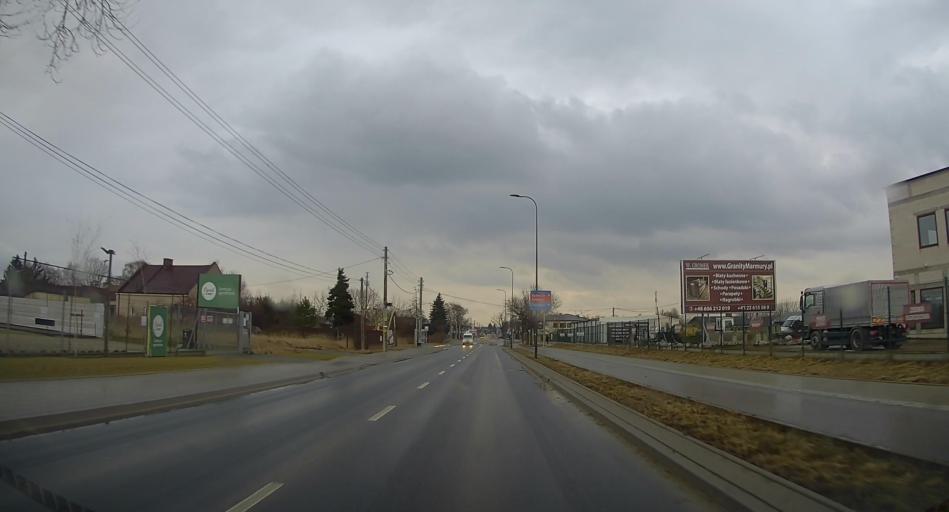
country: PL
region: Masovian Voivodeship
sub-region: Warszawa
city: Wawer
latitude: 52.1950
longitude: 21.1373
